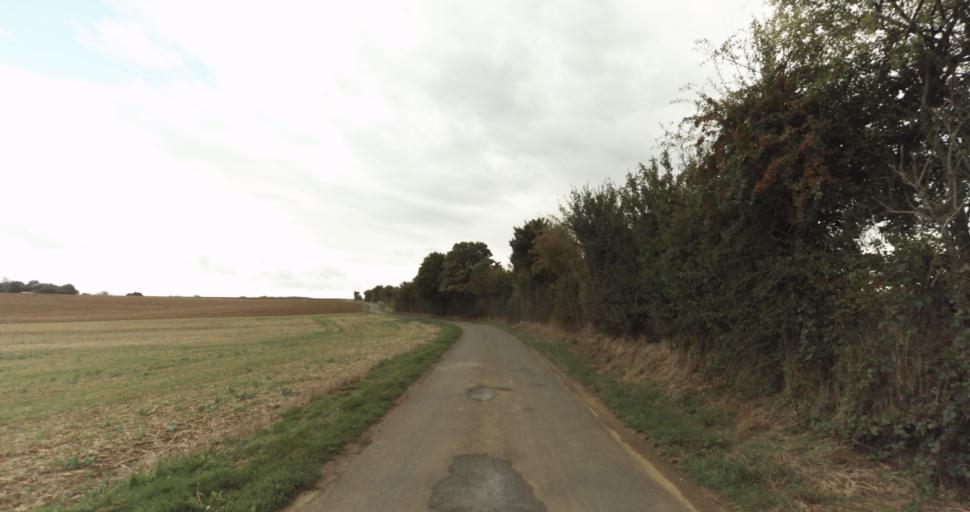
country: FR
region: Lower Normandy
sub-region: Departement de l'Orne
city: Sainte-Gauburge-Sainte-Colombe
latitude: 48.7349
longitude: 0.4047
